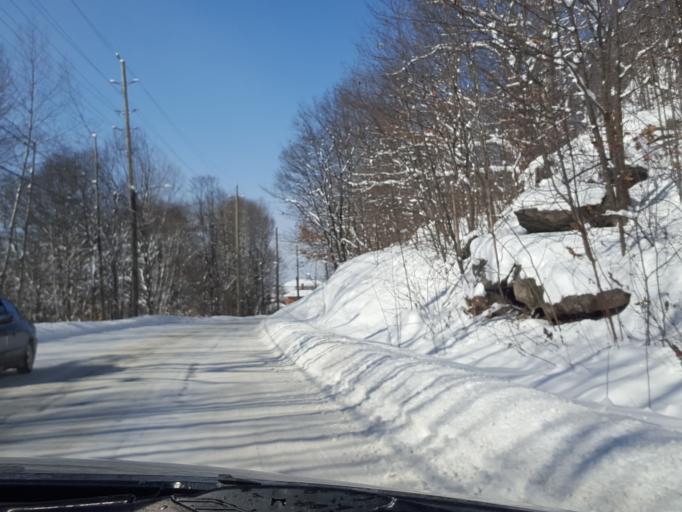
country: CA
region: Ontario
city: Gravenhurst
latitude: 44.9163
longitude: -79.3801
